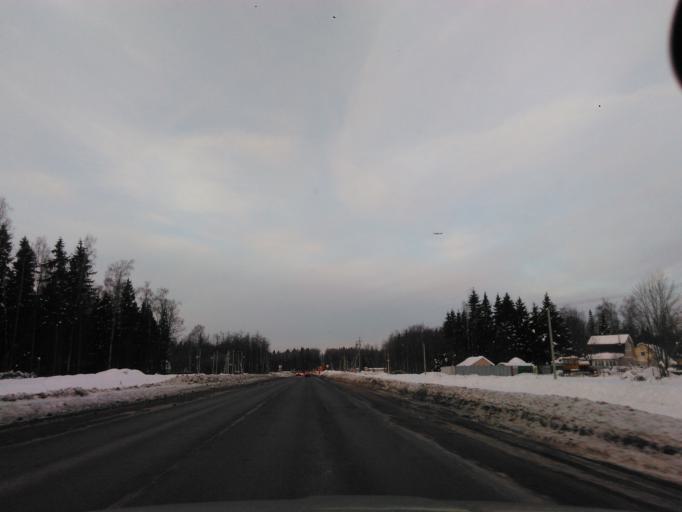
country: RU
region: Moskovskaya
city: Povarovo
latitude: 56.0224
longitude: 37.0413
